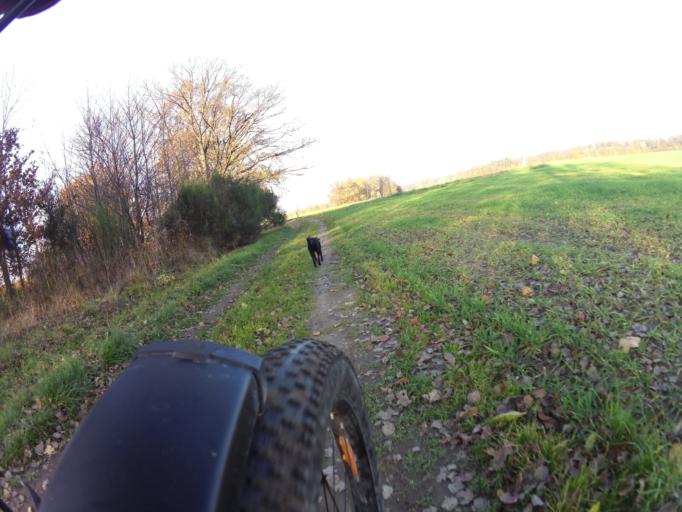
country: PL
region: Pomeranian Voivodeship
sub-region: Powiat pucki
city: Krokowa
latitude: 54.7316
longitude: 18.1977
